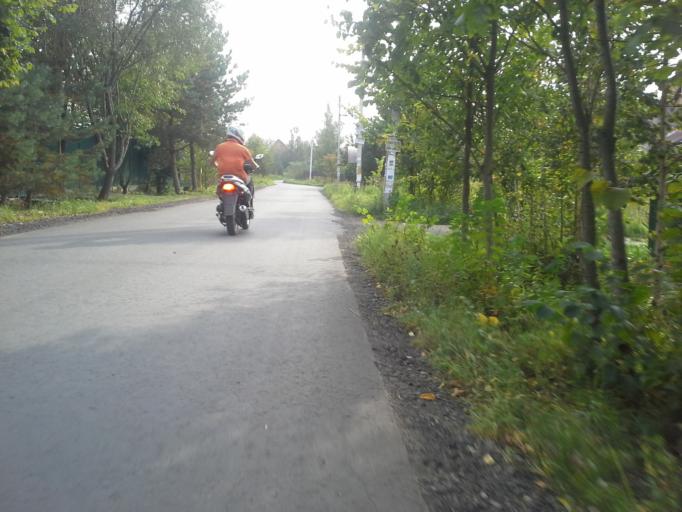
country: RU
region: Moskovskaya
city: Aprelevka
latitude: 55.5593
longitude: 37.0619
